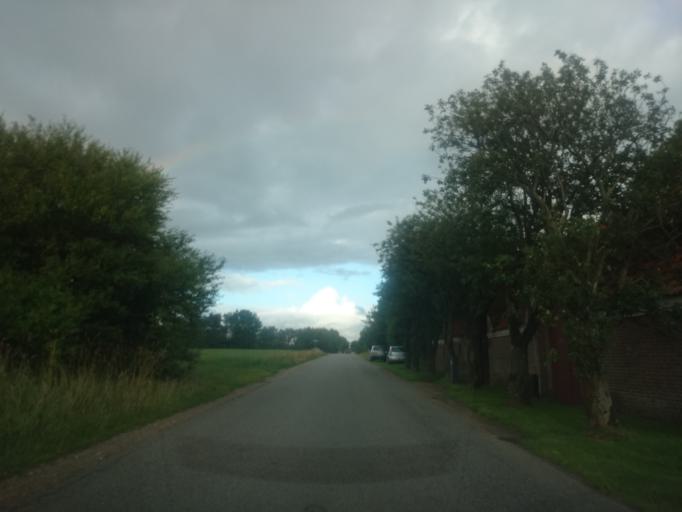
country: DK
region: South Denmark
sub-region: Billund Kommune
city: Grindsted
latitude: 55.6483
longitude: 8.8324
